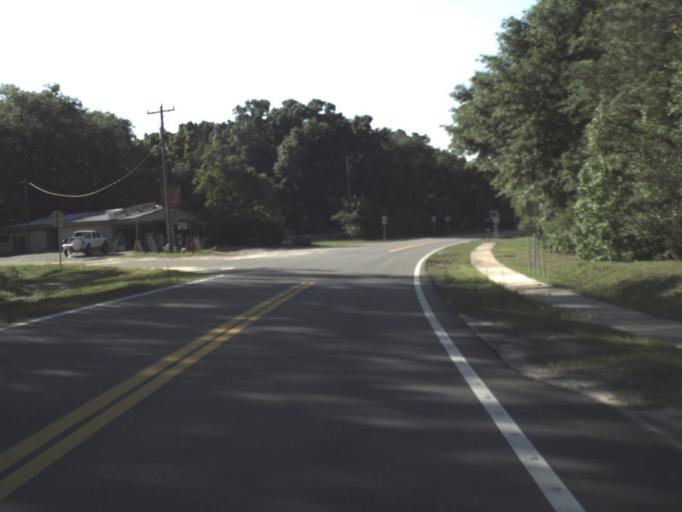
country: US
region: Florida
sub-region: Gulf County
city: Wewahitchka
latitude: 30.0271
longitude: -84.9826
